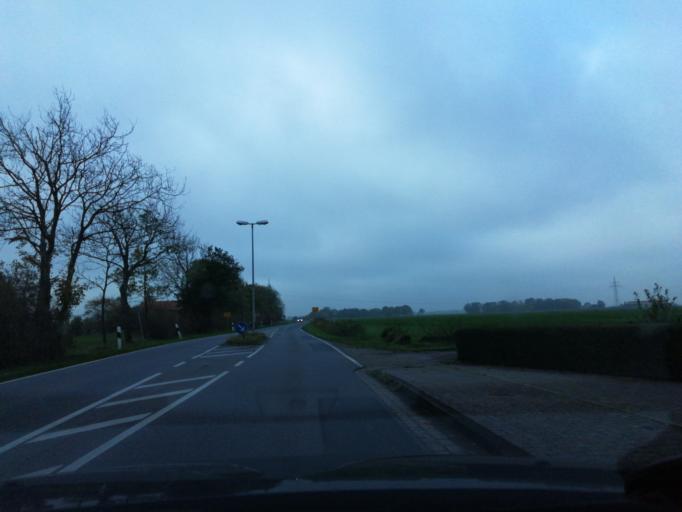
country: DE
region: Lower Saxony
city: Jever
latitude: 53.6719
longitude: 7.8639
